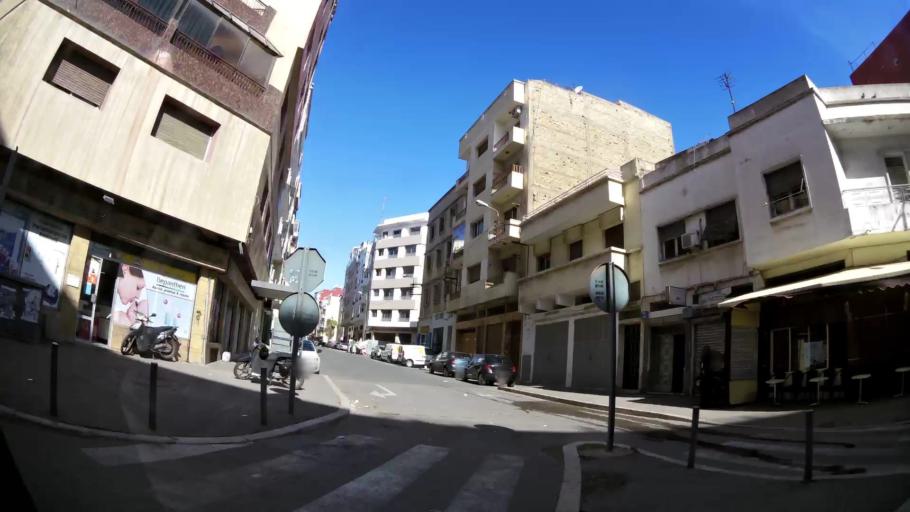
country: MA
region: Grand Casablanca
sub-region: Casablanca
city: Casablanca
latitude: 33.5947
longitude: -7.5867
